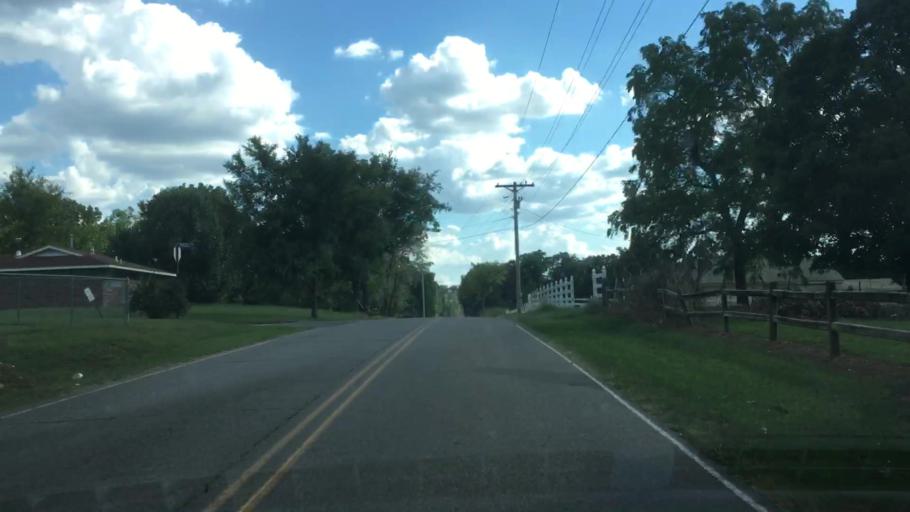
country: US
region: Oklahoma
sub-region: Cherokee County
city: Park Hill
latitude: 35.8063
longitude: -95.0739
